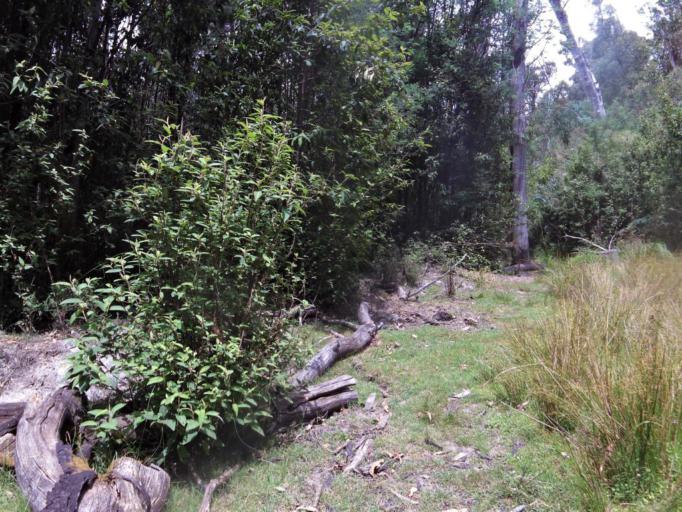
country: AU
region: Victoria
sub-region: Yarra Ranges
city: Healesville
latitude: -37.4409
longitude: 145.5789
